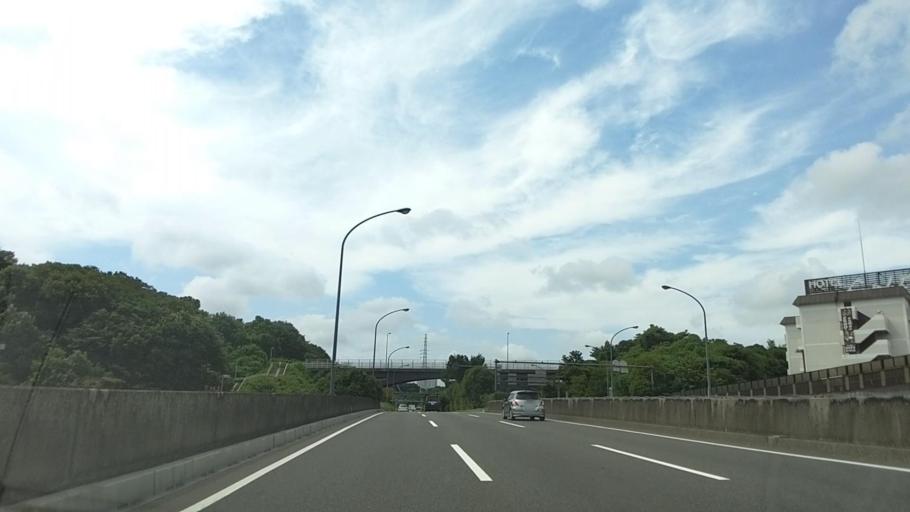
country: JP
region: Kanagawa
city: Yokohama
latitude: 35.4423
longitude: 139.5604
